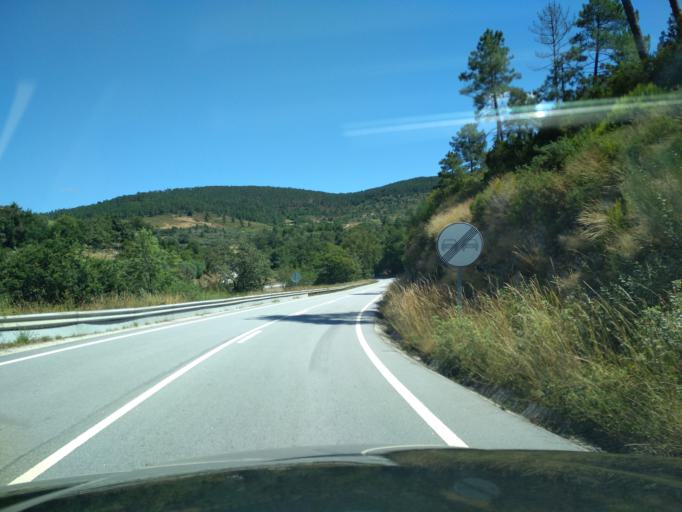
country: PT
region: Vila Real
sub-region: Ribeira de Pena
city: Ribeira de Pena
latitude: 41.5033
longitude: -7.7662
